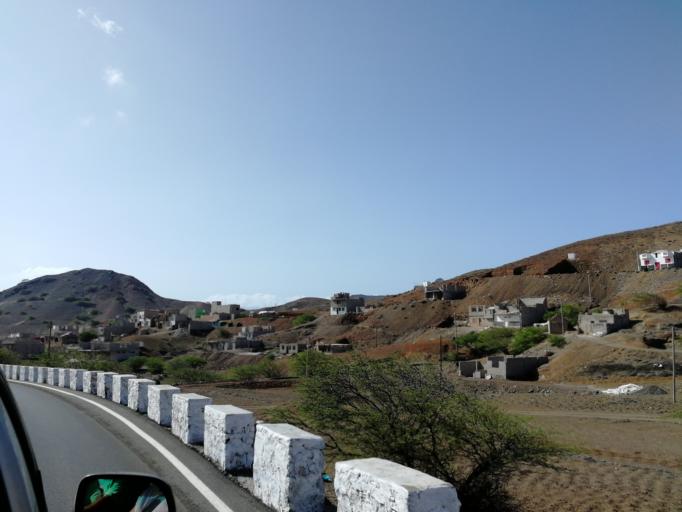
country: CV
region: Sao Vicente
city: Mindelo
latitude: 16.8803
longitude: -24.9671
